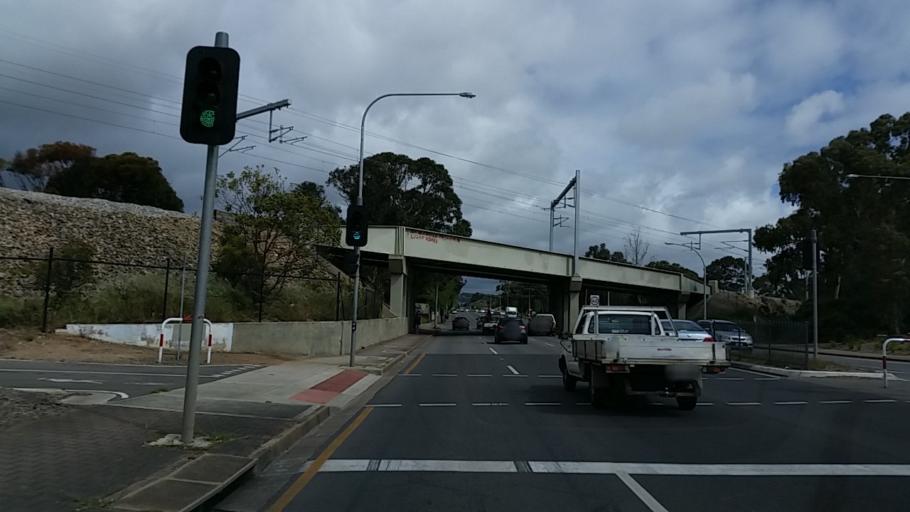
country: AU
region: South Australia
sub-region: Marion
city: Clovelly Park
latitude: -34.9948
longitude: 138.5572
